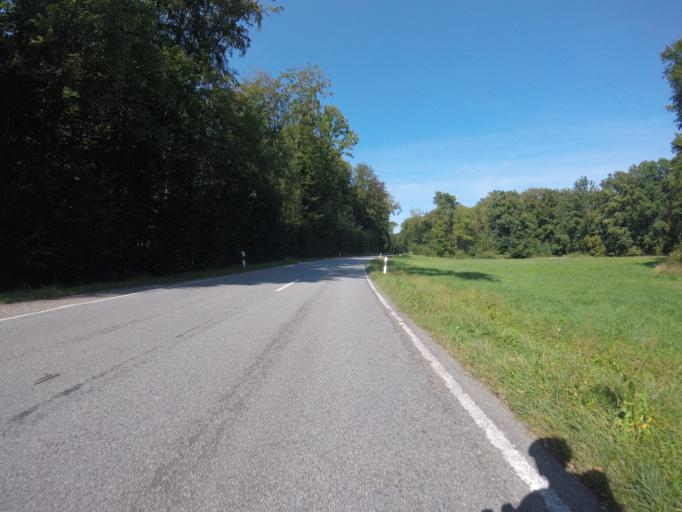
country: DE
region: Baden-Wuerttemberg
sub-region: Regierungsbezirk Stuttgart
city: Ilsfeld
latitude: 49.0311
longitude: 9.2441
